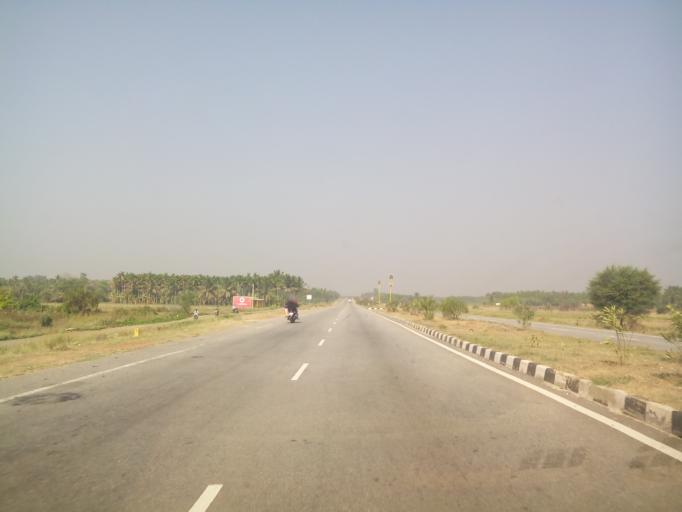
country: IN
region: Karnataka
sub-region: Tumkur
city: Kunigal
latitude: 13.0051
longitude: 76.9993
